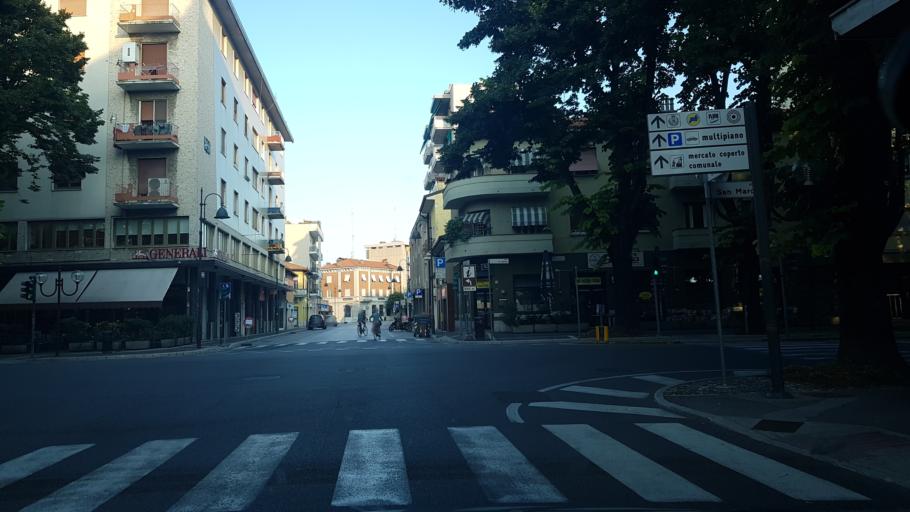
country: IT
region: Friuli Venezia Giulia
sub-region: Provincia di Gorizia
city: Monfalcone
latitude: 45.8074
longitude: 13.5355
